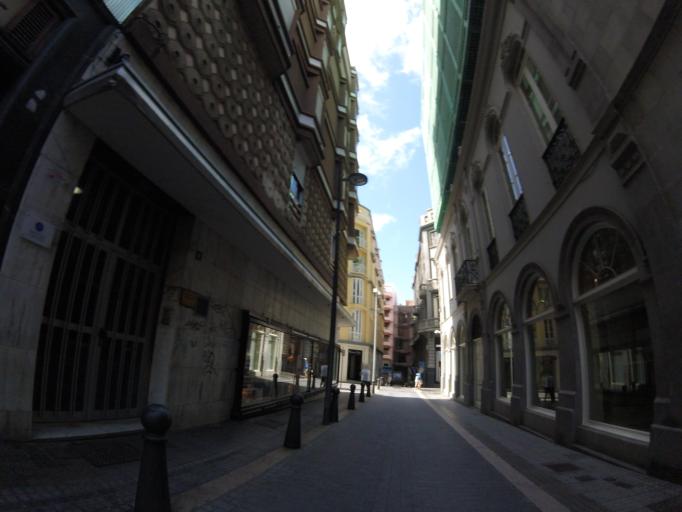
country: ES
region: Canary Islands
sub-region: Provincia de Santa Cruz de Tenerife
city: Santa Cruz de Tenerife
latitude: 28.4674
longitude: -16.2518
